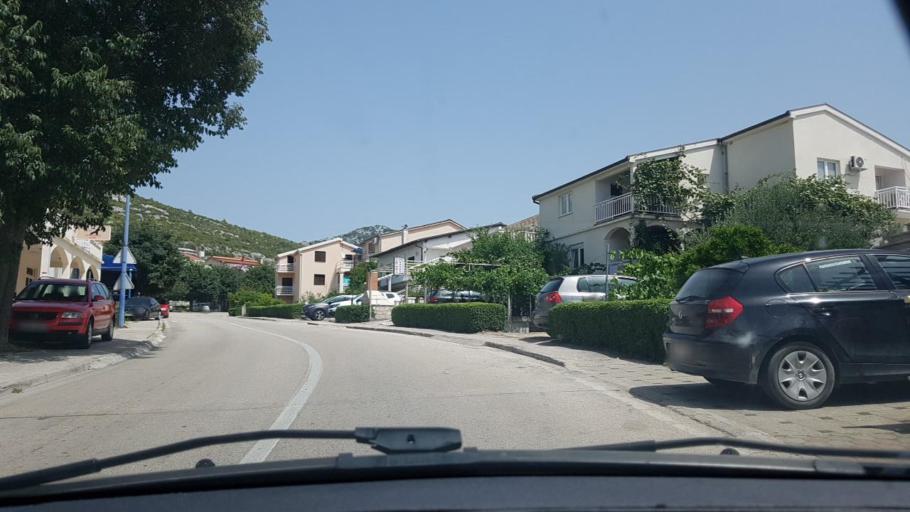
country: BA
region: Federation of Bosnia and Herzegovina
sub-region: Hercegovacko-Bosanski Kanton
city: Neum
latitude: 42.9280
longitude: 17.6164
